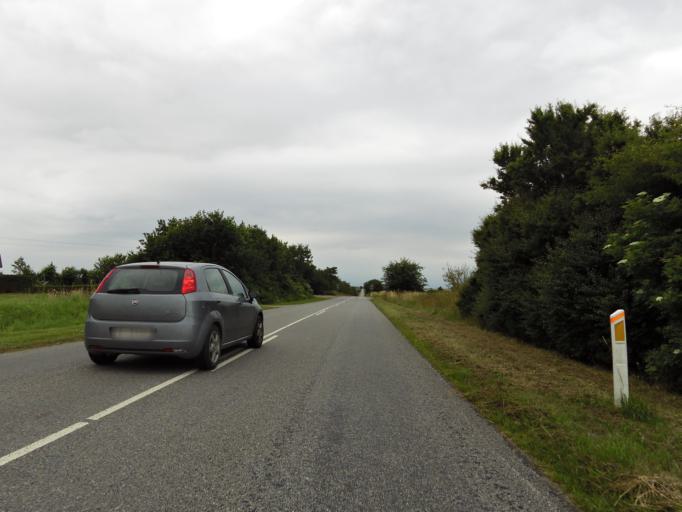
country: DK
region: South Denmark
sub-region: Tonder Kommune
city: Logumkloster
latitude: 55.1223
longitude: 8.9654
